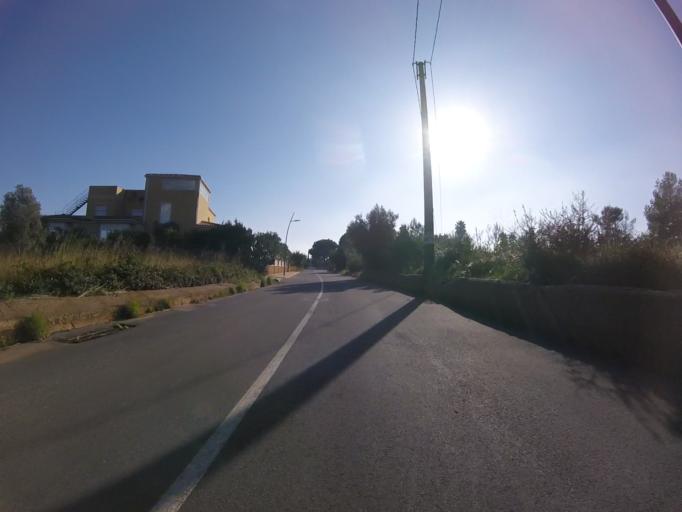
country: ES
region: Valencia
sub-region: Provincia de Castello
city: Peniscola
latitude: 40.3836
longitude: 0.3812
